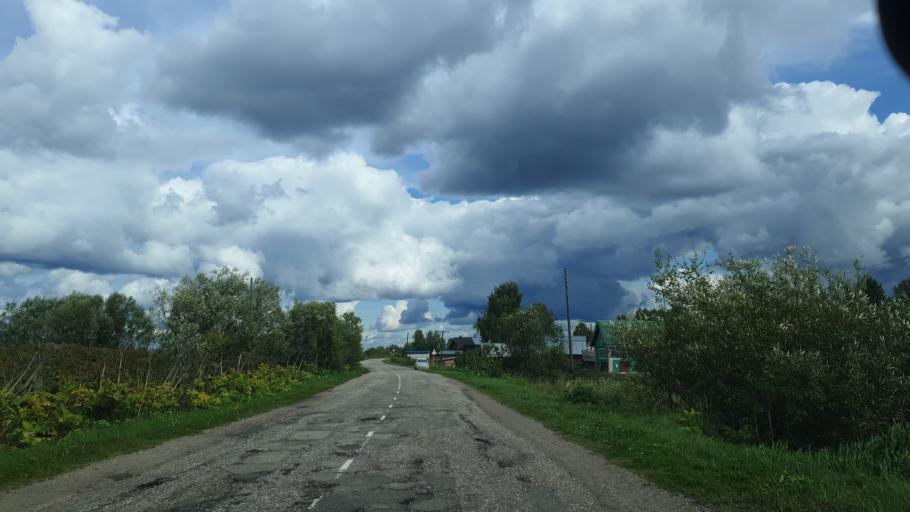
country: RU
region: Komi Republic
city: Aykino
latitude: 61.9535
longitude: 50.1772
